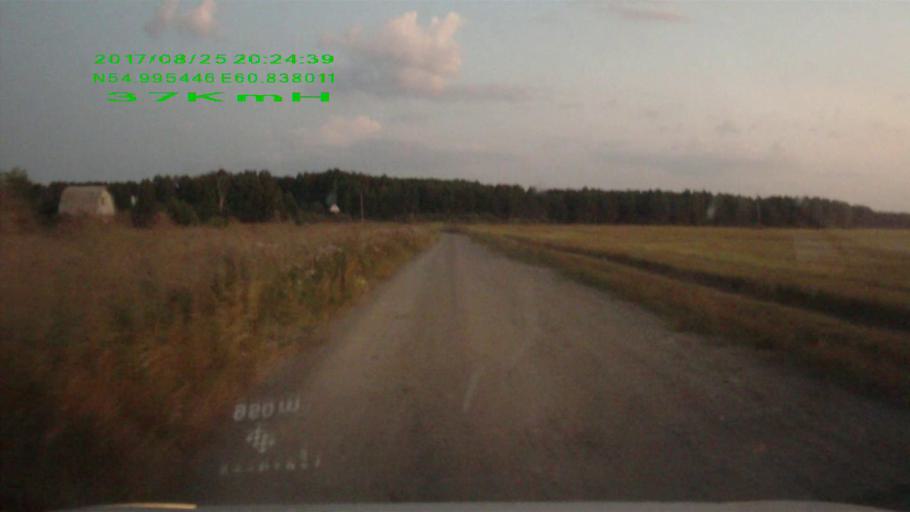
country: RU
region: Chelyabinsk
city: Timiryazevskiy
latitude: 54.9952
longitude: 60.8380
